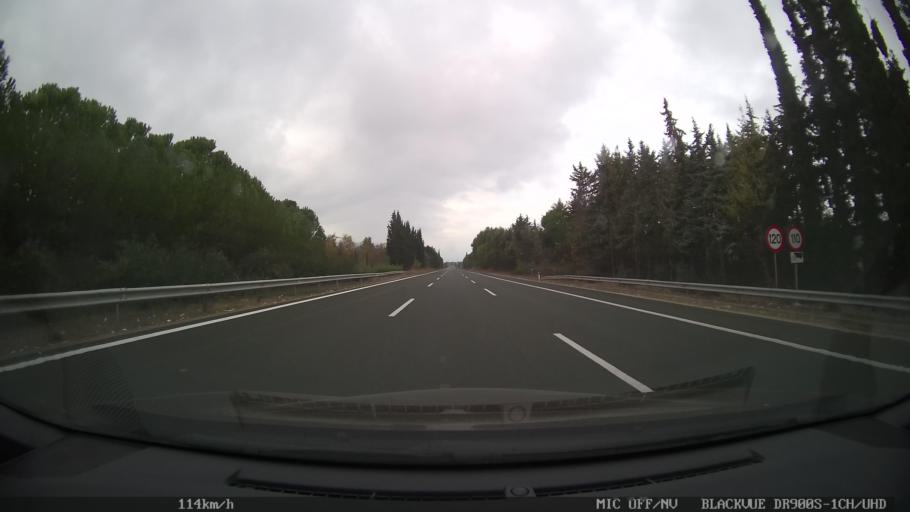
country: GR
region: Central Macedonia
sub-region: Nomos Pierias
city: Korinos
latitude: 40.3415
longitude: 22.5893
